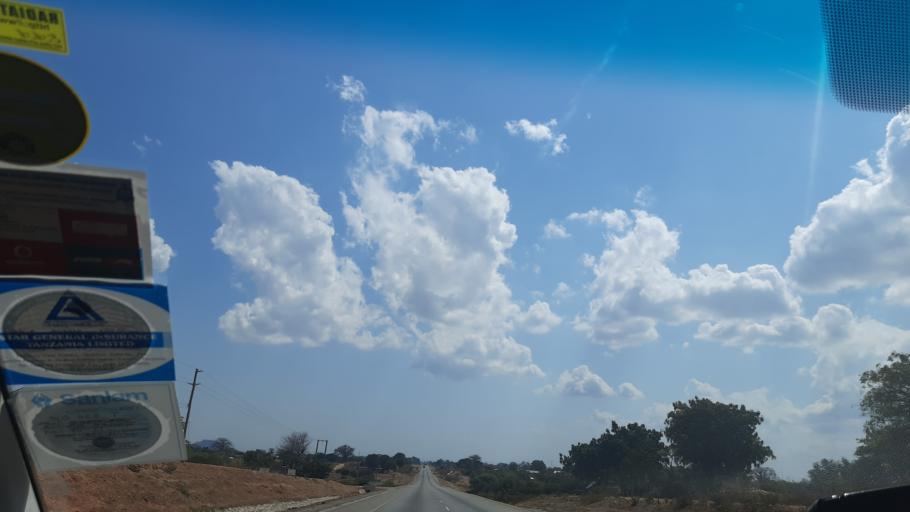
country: TZ
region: Singida
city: Kintinku
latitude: -6.0120
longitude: 35.4274
